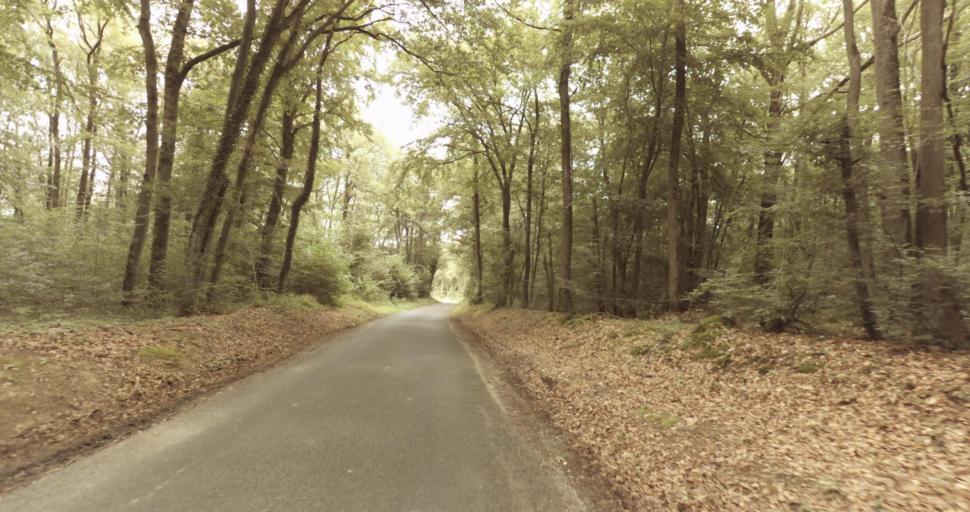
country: FR
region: Haute-Normandie
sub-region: Departement de l'Eure
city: Menilles
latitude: 49.0328
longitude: 1.3127
